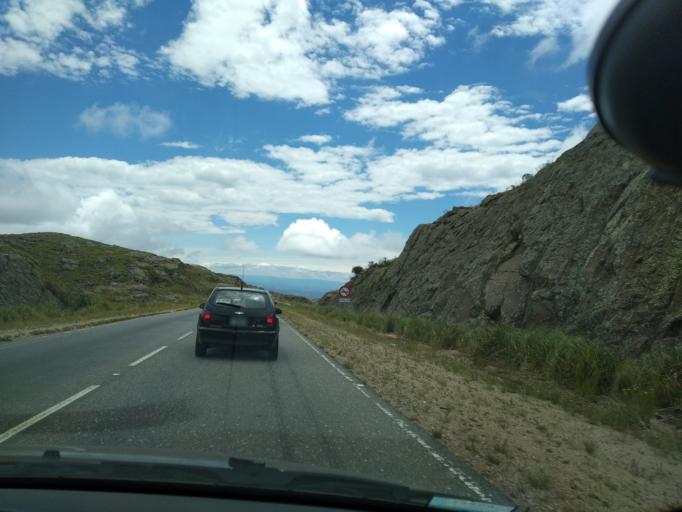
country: AR
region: Cordoba
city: Cuesta Blanca
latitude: -31.6140
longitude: -64.7407
